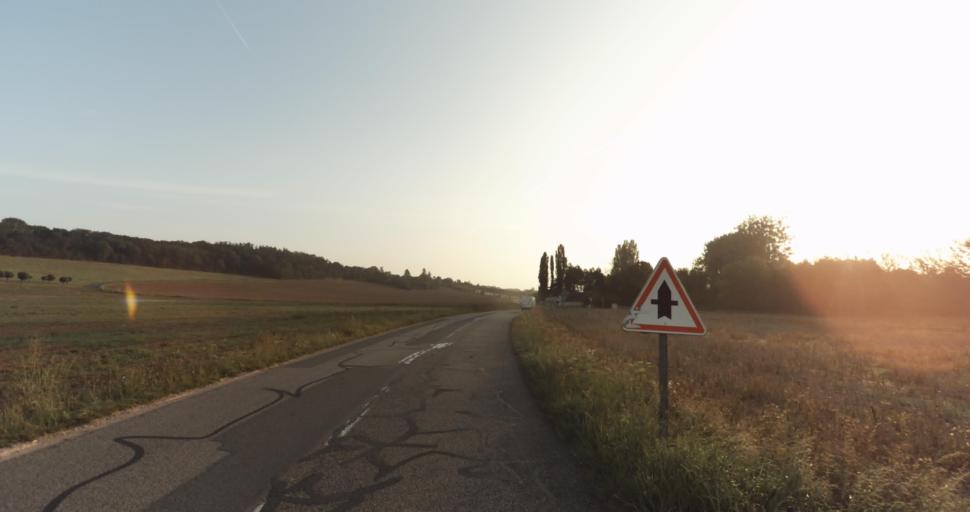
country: FR
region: Haute-Normandie
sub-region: Departement de l'Eure
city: Marcilly-sur-Eure
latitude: 48.7786
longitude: 1.3395
